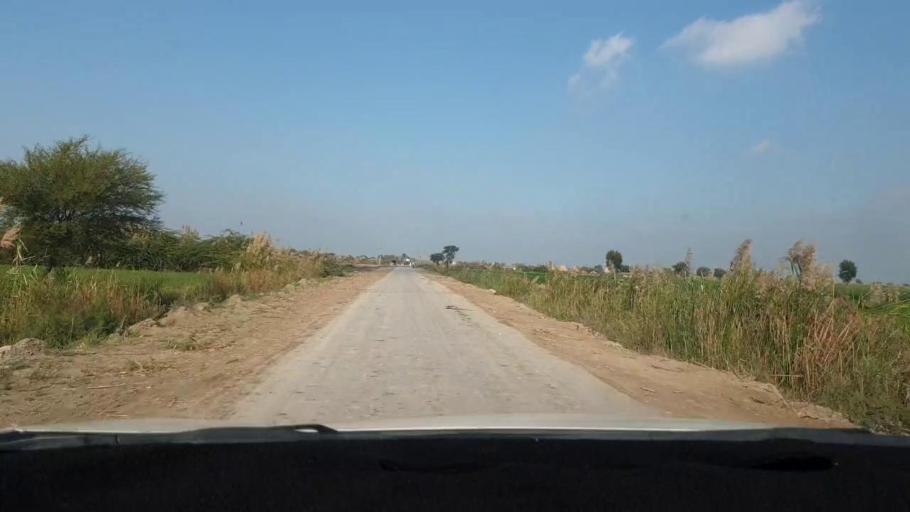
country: PK
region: Sindh
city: Berani
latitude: 25.7965
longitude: 68.8367
